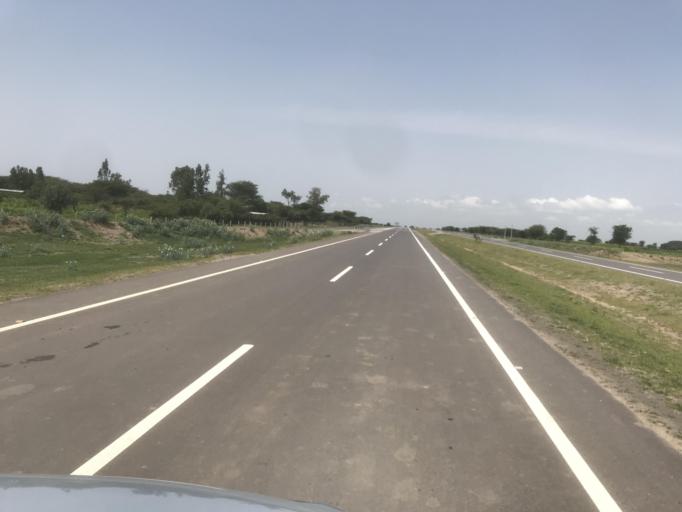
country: ET
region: Oromiya
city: Mojo
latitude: 8.3015
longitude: 38.9357
